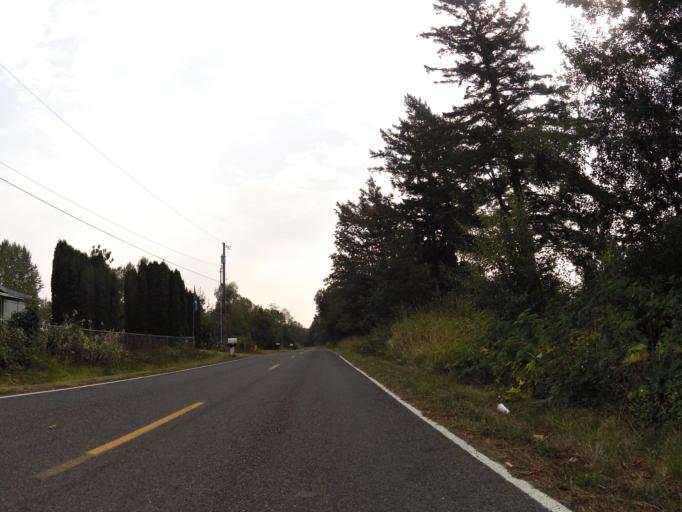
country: US
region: Washington
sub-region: Whatcom County
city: Ferndale
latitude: 48.8071
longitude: -122.6718
